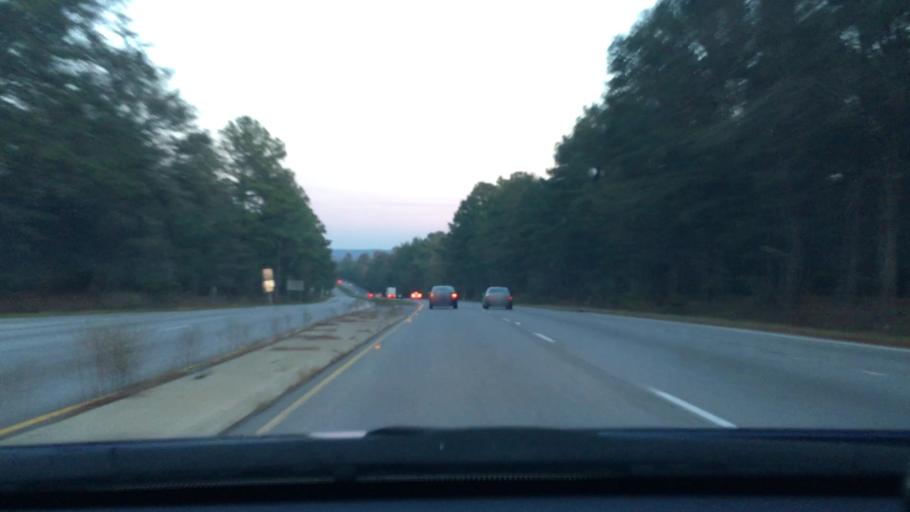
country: US
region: South Carolina
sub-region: Richland County
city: Gadsden
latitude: 33.9424
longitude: -80.6832
